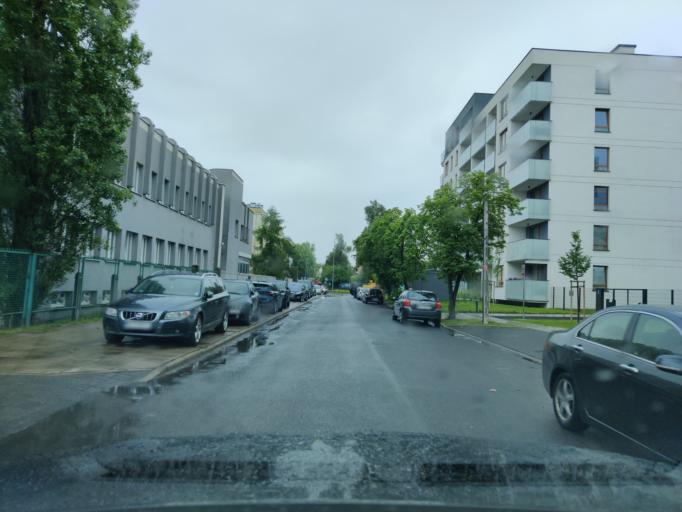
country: PL
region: Masovian Voivodeship
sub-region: Warszawa
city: Praga Poludnie
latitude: 52.2535
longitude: 21.0773
